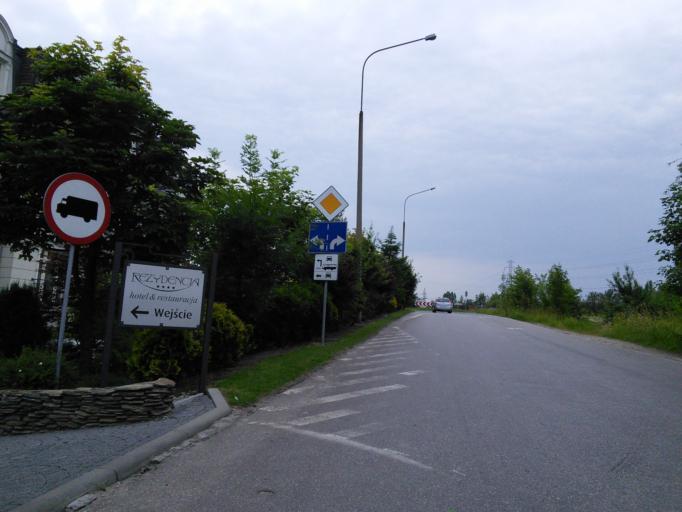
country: PL
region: Silesian Voivodeship
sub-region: Bytom
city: Bytom
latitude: 50.3616
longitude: 18.9372
